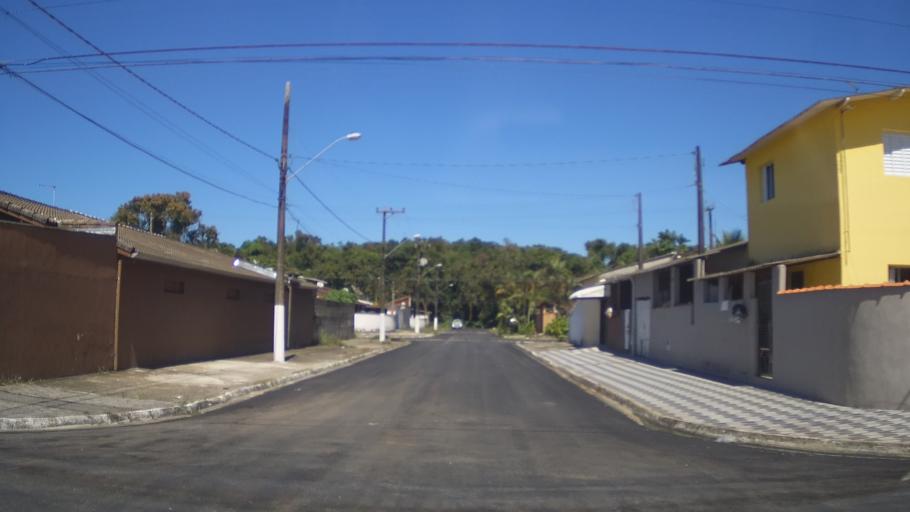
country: BR
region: Sao Paulo
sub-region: Mongagua
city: Mongagua
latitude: -24.0759
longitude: -46.5957
